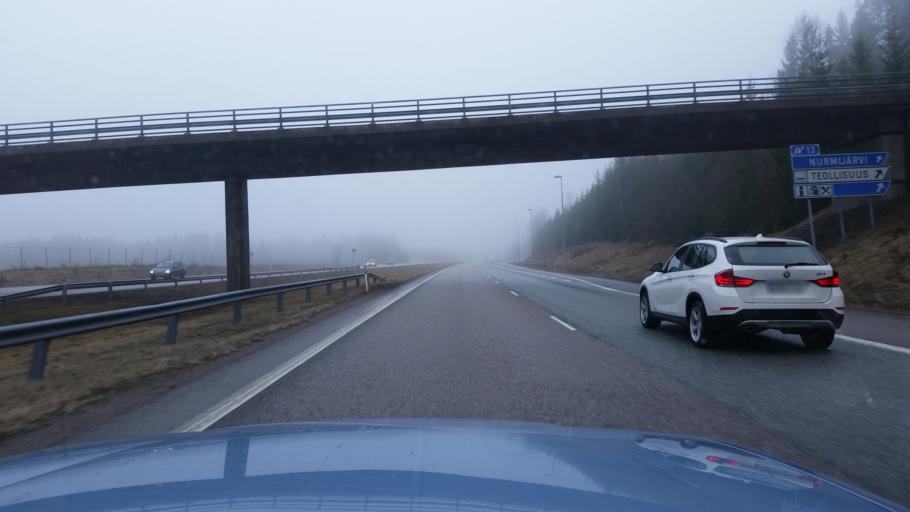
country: FI
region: Uusimaa
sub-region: Helsinki
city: Nurmijaervi
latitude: 60.4630
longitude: 24.8489
